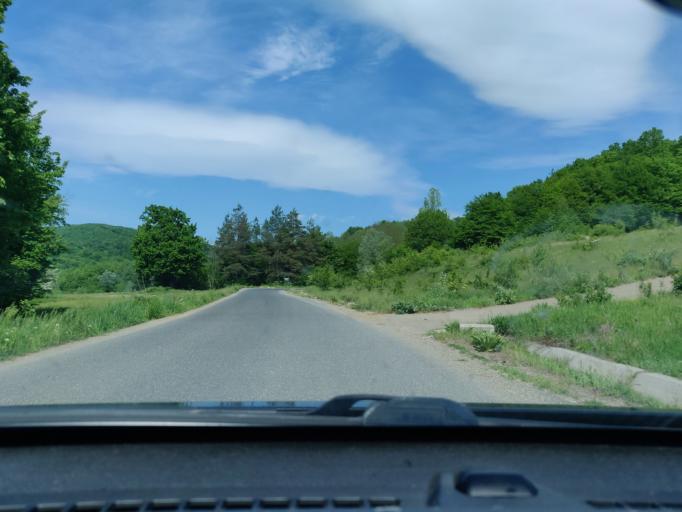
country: RO
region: Vrancea
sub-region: Comuna Vidra
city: Vidra
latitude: 45.9317
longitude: 26.8904
